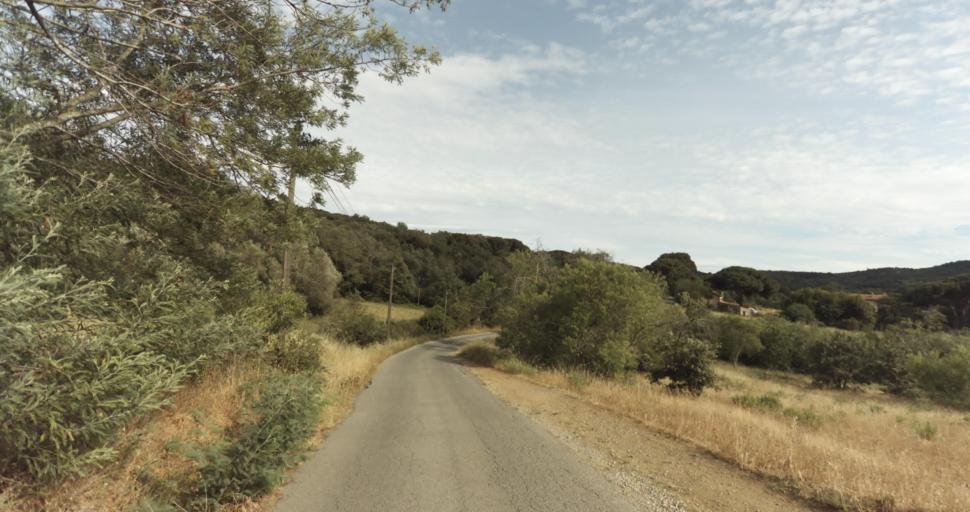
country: FR
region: Provence-Alpes-Cote d'Azur
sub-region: Departement du Var
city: Gassin
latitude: 43.2229
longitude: 6.5800
